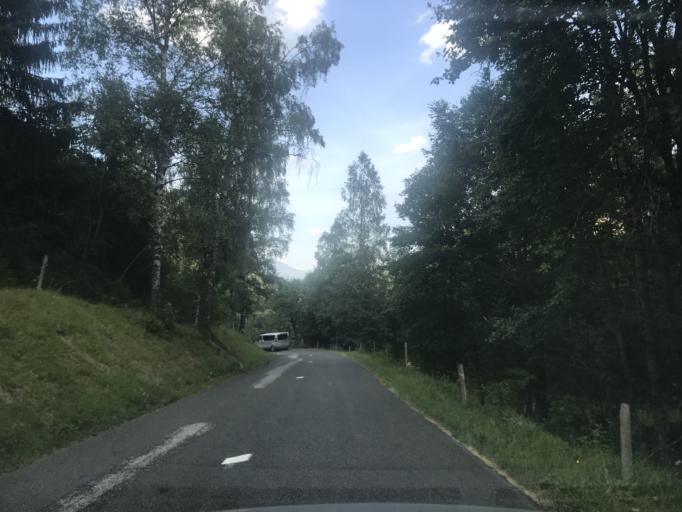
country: FR
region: Rhone-Alpes
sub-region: Departement de la Savoie
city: Saint-Etienne-de-Cuines
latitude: 45.2708
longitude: 6.2004
